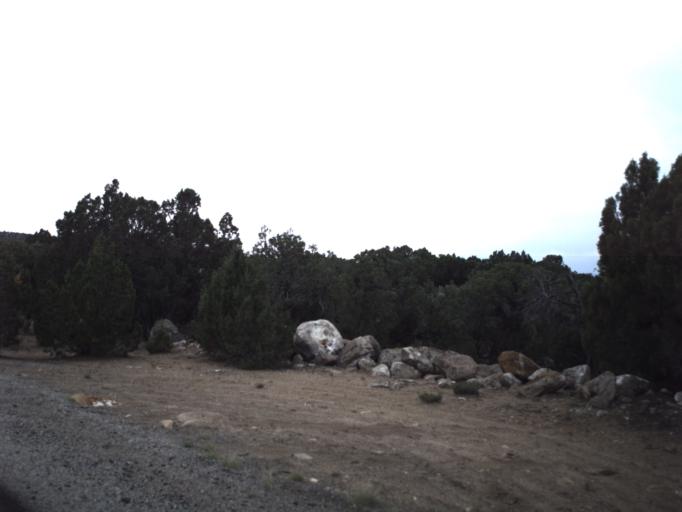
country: US
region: Utah
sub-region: Carbon County
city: East Carbon City
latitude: 39.4641
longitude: -110.3932
